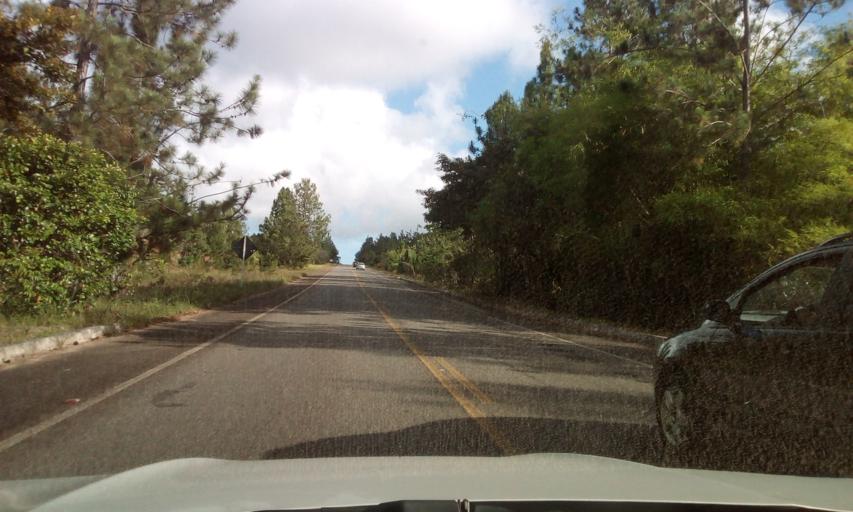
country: BR
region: Bahia
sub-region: Entre Rios
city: Entre Rios
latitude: -12.1382
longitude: -37.7915
